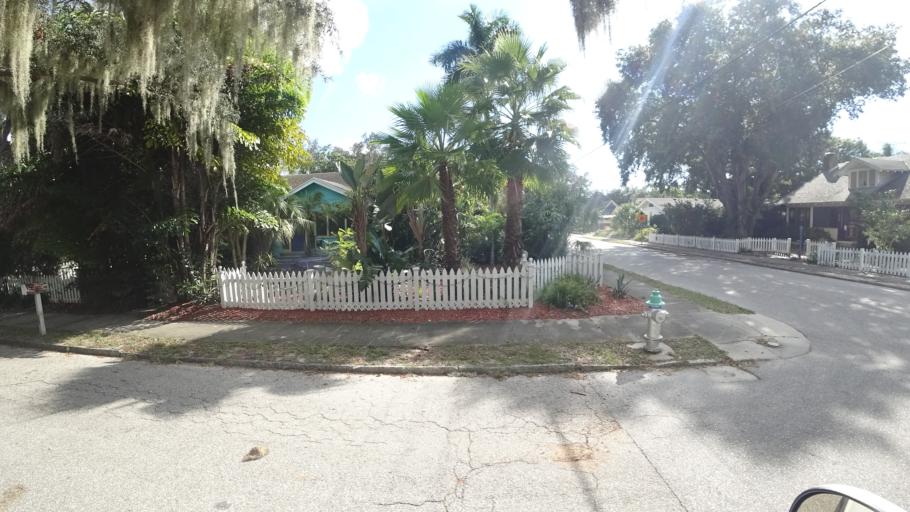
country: US
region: Florida
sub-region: Manatee County
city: Bradenton
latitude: 27.4946
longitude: -82.5832
